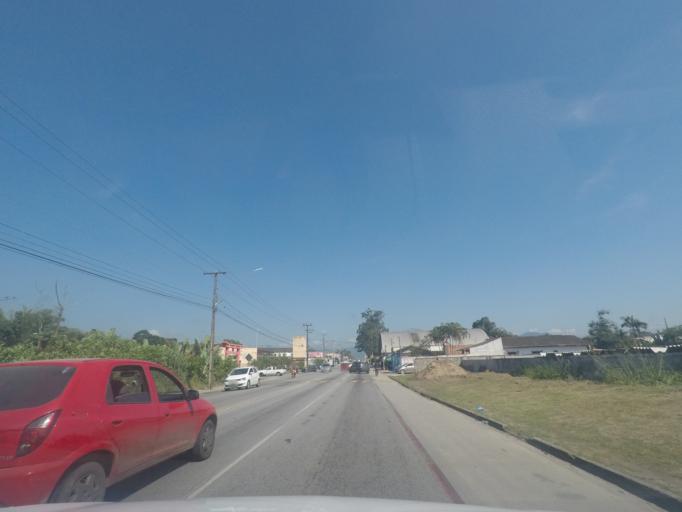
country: BR
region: Parana
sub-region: Paranagua
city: Paranagua
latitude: -25.5504
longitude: -48.5479
